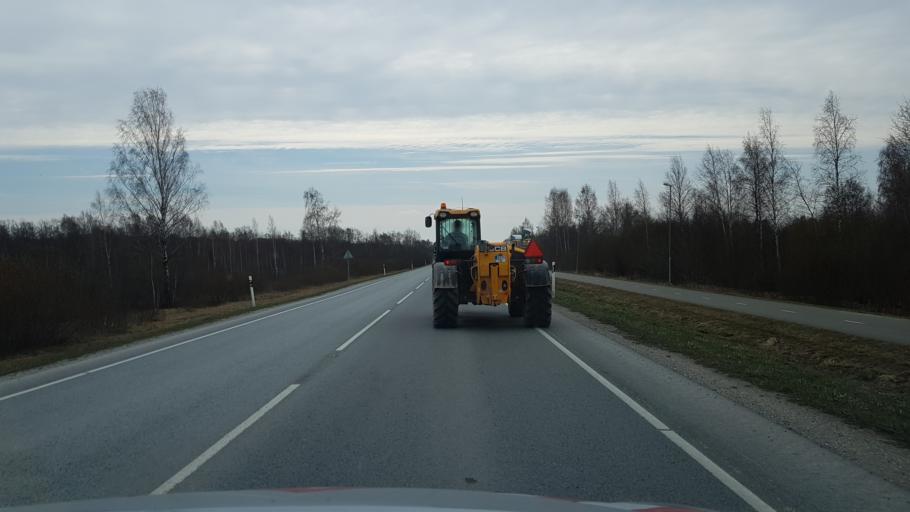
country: EE
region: Laeaene-Virumaa
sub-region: Rakvere linn
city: Rakvere
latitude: 59.3451
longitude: 26.3410
